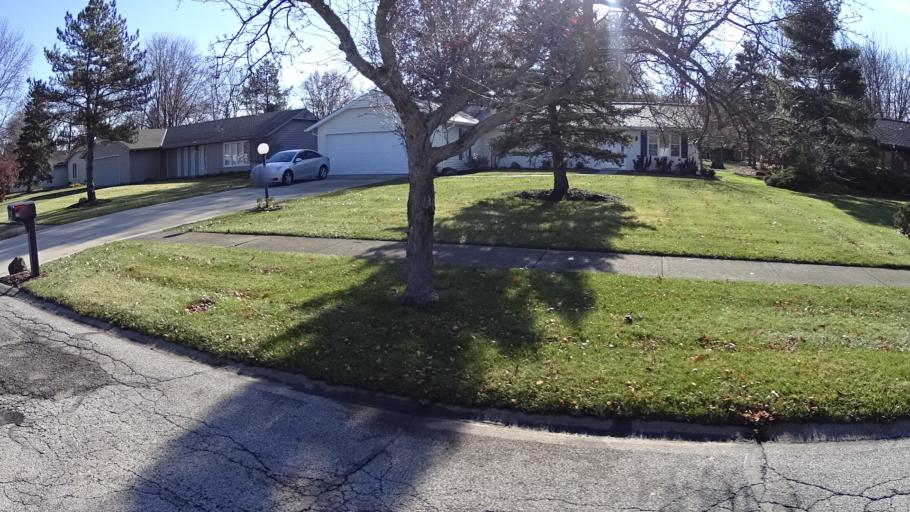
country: US
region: Ohio
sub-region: Lorain County
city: North Ridgeville
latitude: 41.4177
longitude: -81.9851
